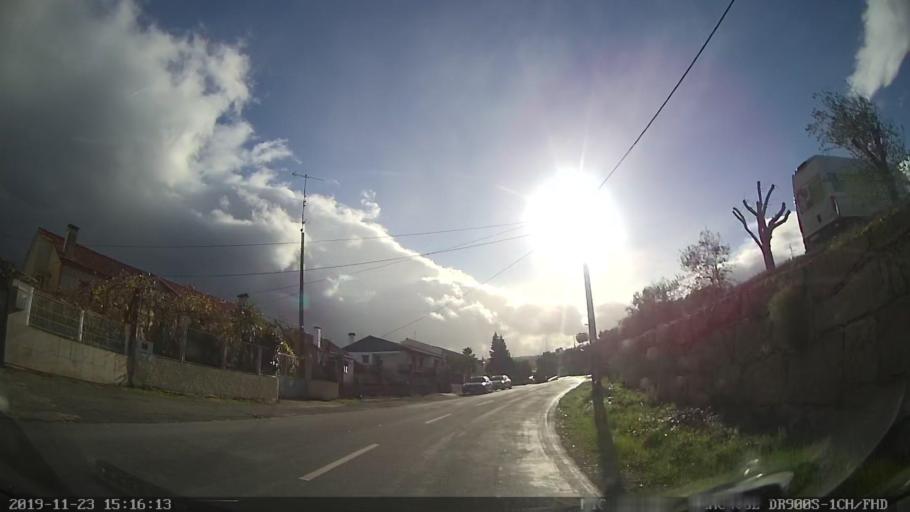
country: PT
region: Vila Real
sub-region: Peso da Regua
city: Peso da Regua
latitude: 41.1281
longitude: -7.7839
